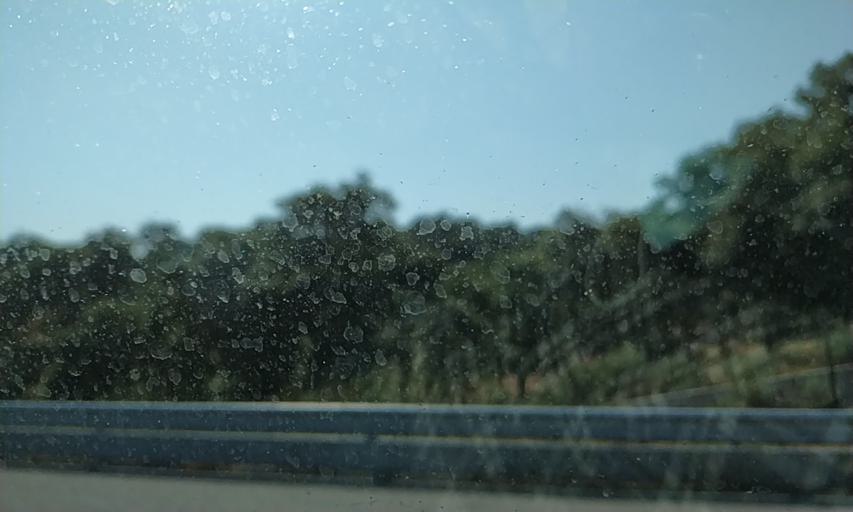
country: PT
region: Braganca
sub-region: Macedo de Cavaleiros
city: Macedo de Cavaleiros
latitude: 41.5510
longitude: -7.0356
